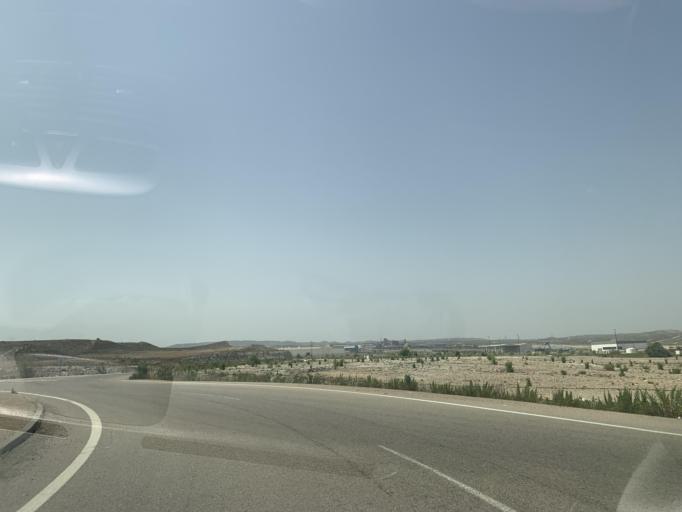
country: ES
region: Aragon
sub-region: Provincia de Zaragoza
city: Zaragoza
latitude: 41.5857
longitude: -0.8288
